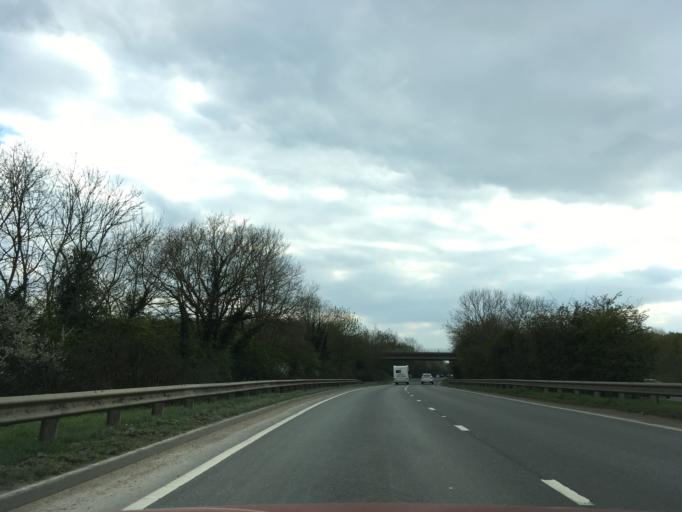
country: GB
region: England
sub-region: Oxfordshire
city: Bicester
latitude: 51.8852
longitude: -1.1704
